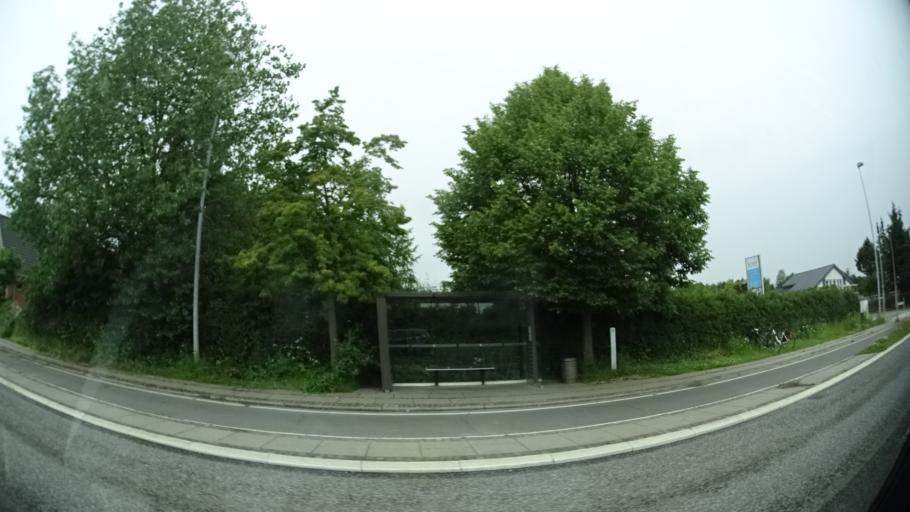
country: DK
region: Central Jutland
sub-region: Arhus Kommune
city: Hjortshoj
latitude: 56.2302
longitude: 10.2939
